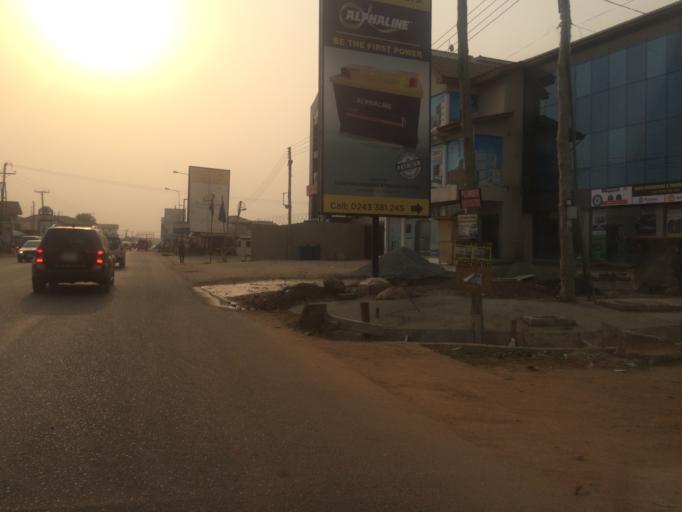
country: GH
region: Greater Accra
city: Nungua
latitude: 5.6355
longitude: -0.1015
